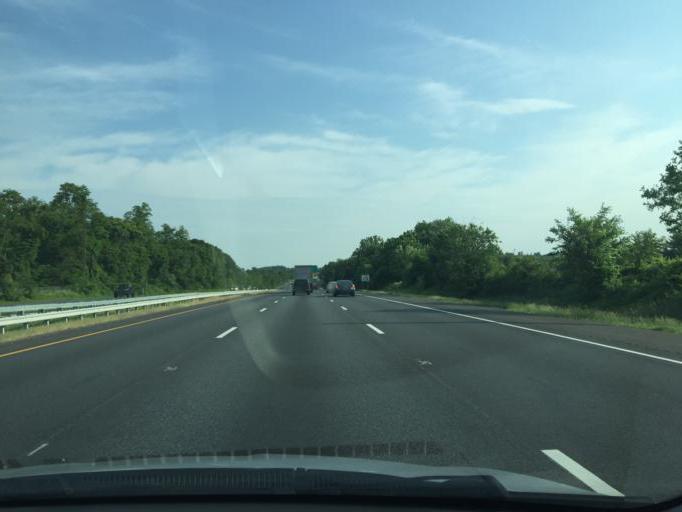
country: US
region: Maryland
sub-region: Baltimore County
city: Cockeysville
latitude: 39.4829
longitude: -76.6652
